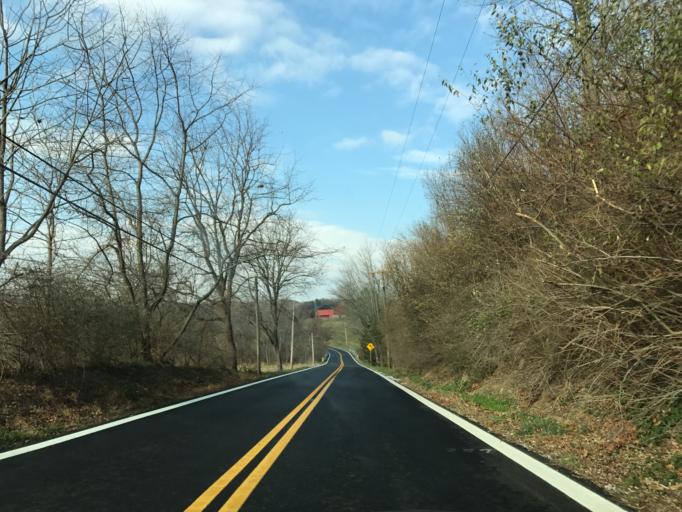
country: US
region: Maryland
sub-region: Baltimore County
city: Hunt Valley
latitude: 39.5844
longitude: -76.5867
